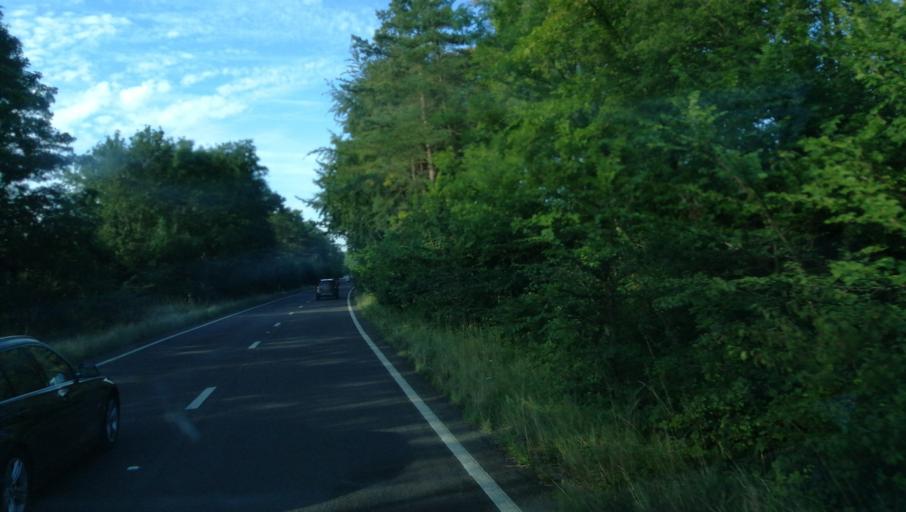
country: GB
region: England
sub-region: Oxfordshire
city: Deddington
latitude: 51.9456
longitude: -1.3220
